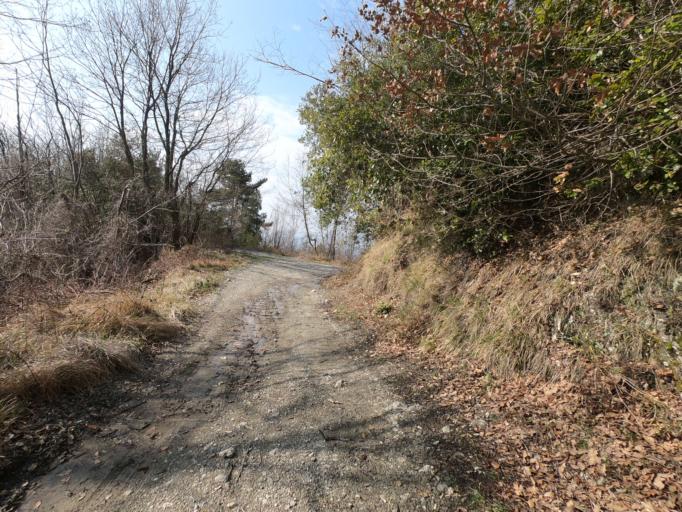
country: IT
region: Liguria
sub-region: Provincia di Savona
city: Castelvecchio di Rocca Barbena
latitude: 44.1258
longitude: 8.1426
